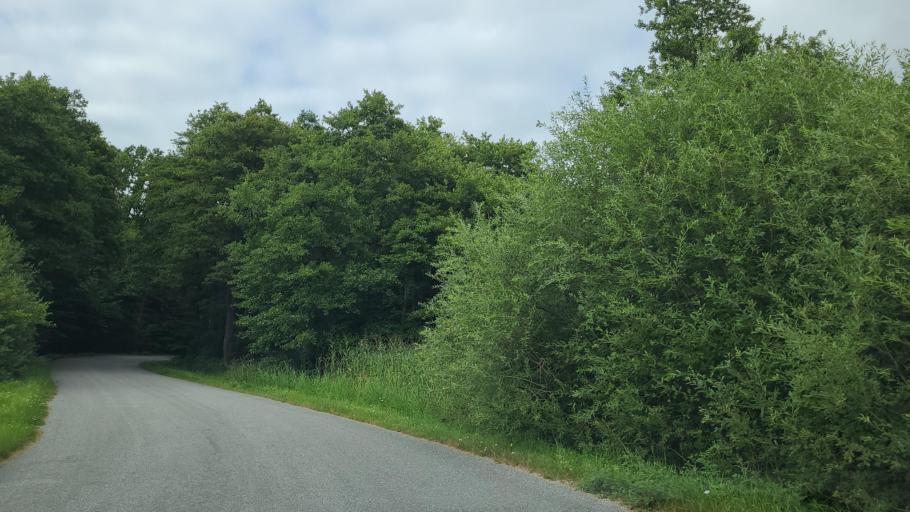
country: SE
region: Stockholm
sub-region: Upplands-Bro Kommun
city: Bro
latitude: 59.4809
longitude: 17.5638
